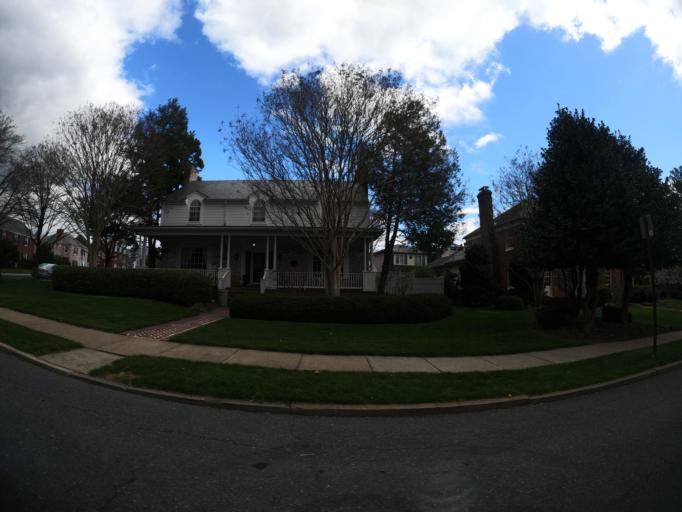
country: US
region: Maryland
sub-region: Frederick County
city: Frederick
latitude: 39.4183
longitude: -77.4245
